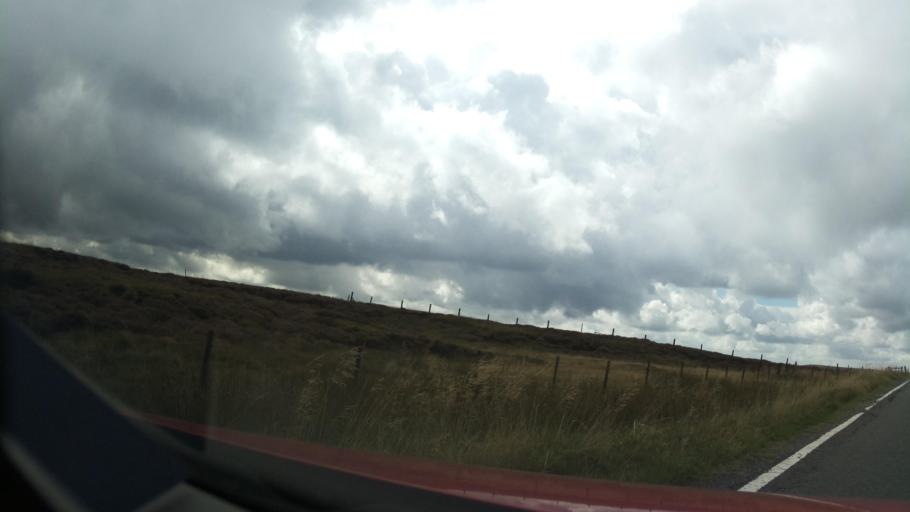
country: GB
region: England
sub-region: Kirklees
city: Meltham
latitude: 53.5301
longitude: -1.8555
